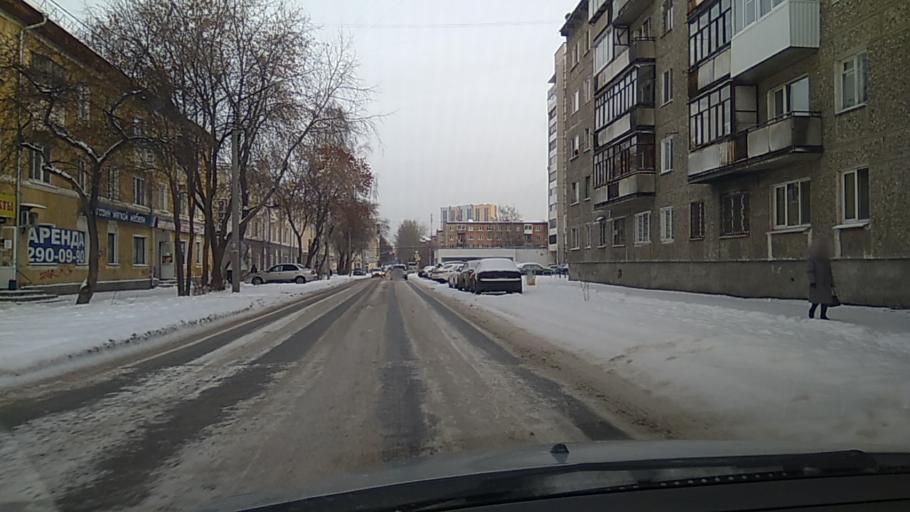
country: RU
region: Sverdlovsk
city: Yekaterinburg
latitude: 56.8979
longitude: 60.5968
